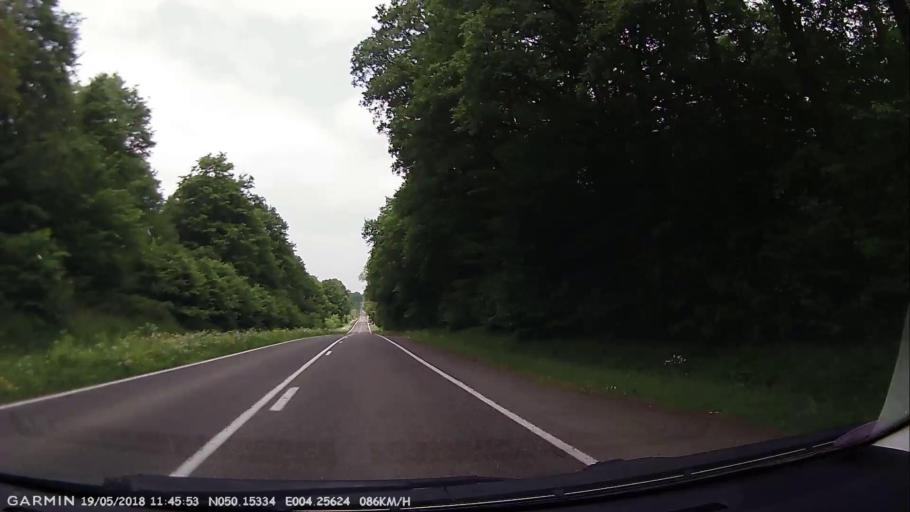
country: BE
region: Wallonia
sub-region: Province du Hainaut
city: Froidchapelle
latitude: 50.1536
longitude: 4.2560
